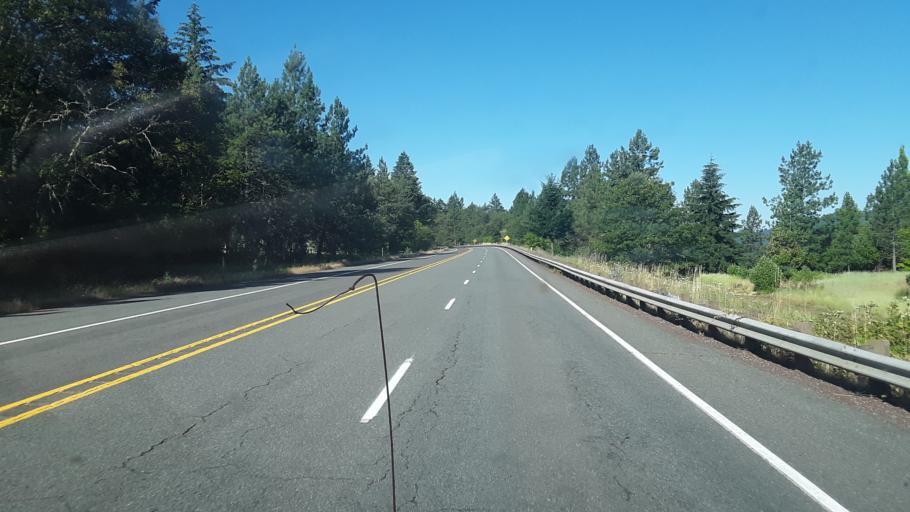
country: US
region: Oregon
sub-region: Jackson County
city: Shady Cove
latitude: 42.6878
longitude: -122.6056
